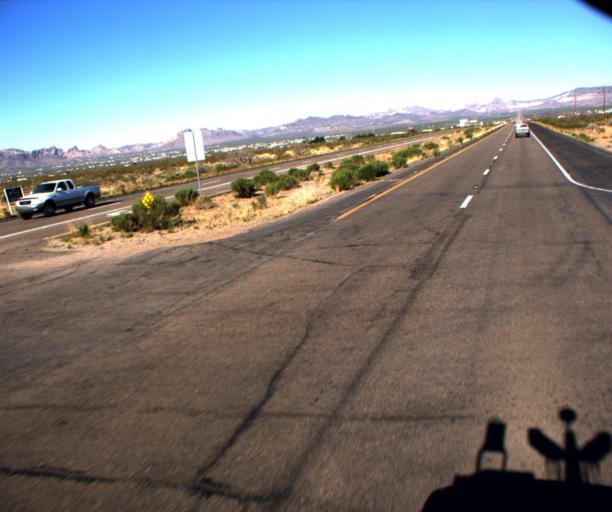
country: US
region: Arizona
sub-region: Mohave County
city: Golden Valley
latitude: 35.2240
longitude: -114.2537
